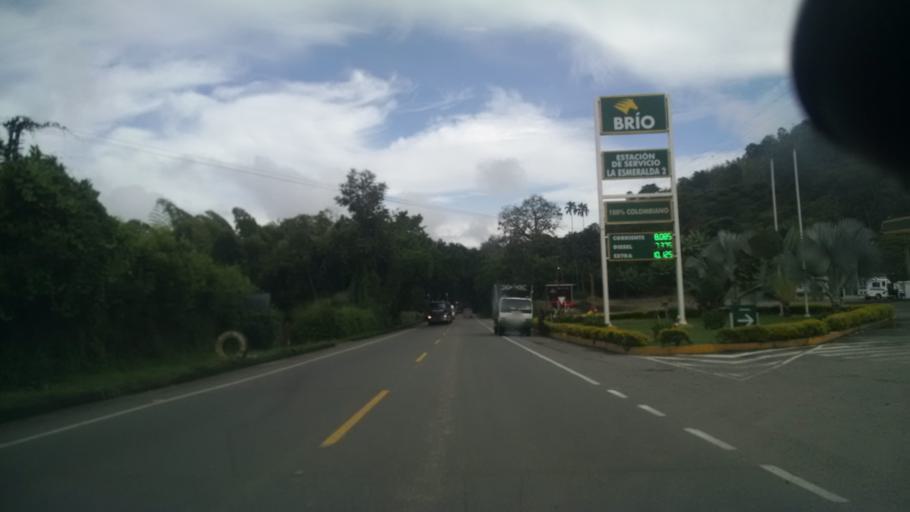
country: CO
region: Caldas
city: Palestina
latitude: 5.0705
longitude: -75.6402
